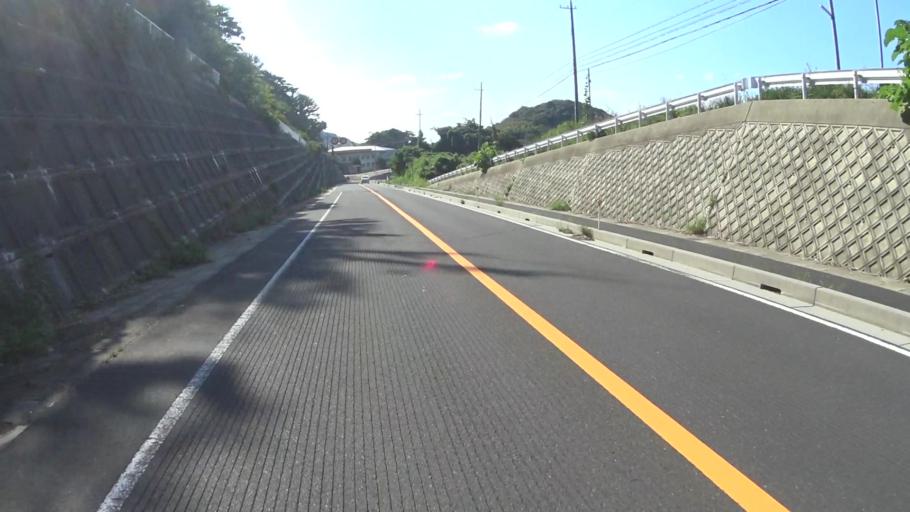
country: JP
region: Kyoto
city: Miyazu
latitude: 35.7414
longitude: 135.1157
